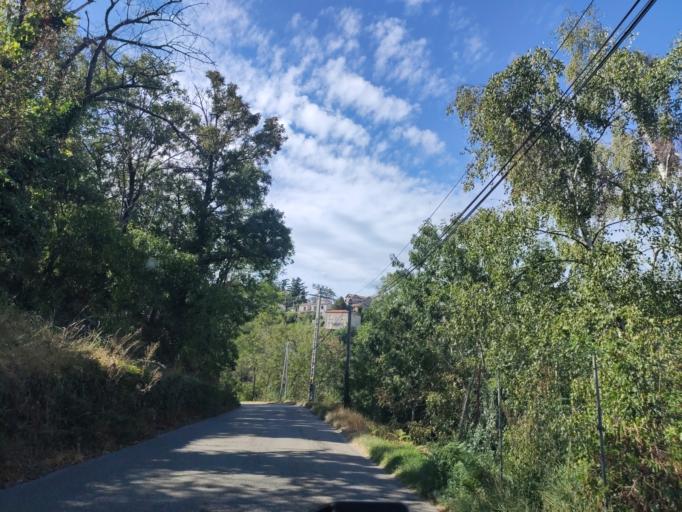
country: FR
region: Rhone-Alpes
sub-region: Departement de la Loire
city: Pelussin
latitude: 45.4146
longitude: 4.6768
